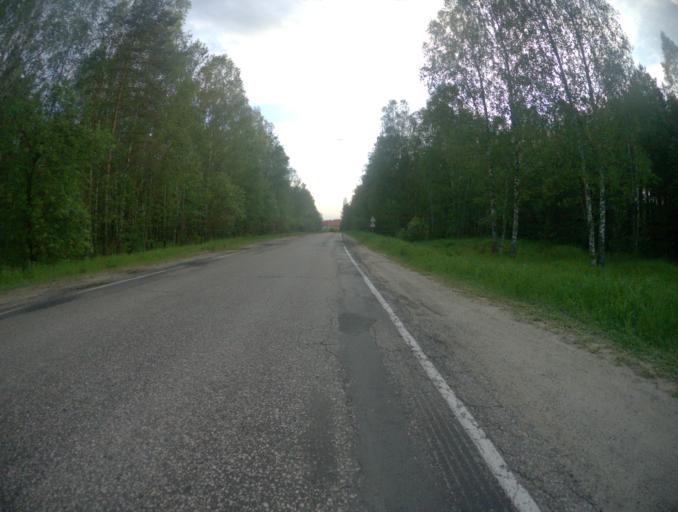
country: RU
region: Vladimir
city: Gus'-Khrustal'nyy
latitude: 55.6359
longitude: 40.7204
